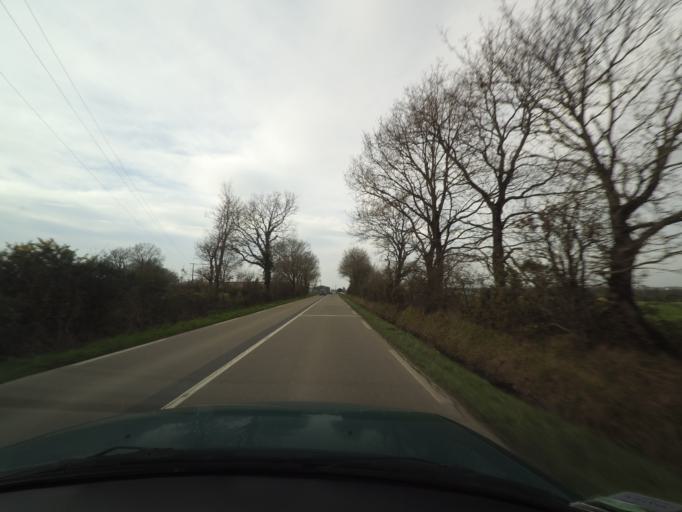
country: FR
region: Pays de la Loire
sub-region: Departement de la Loire-Atlantique
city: Saint-Pere-en-Retz
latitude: 47.1940
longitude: -2.0261
